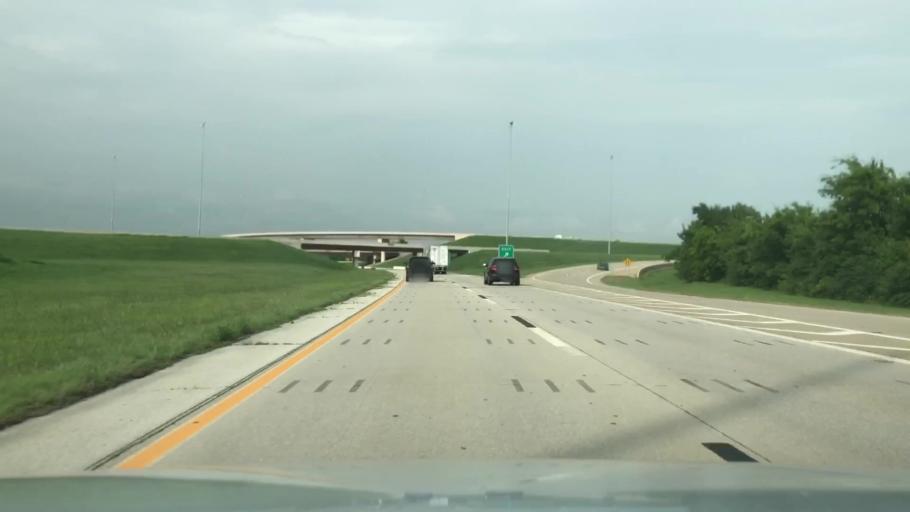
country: US
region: Oklahoma
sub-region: Tulsa County
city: Turley
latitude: 36.1966
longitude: -95.9503
